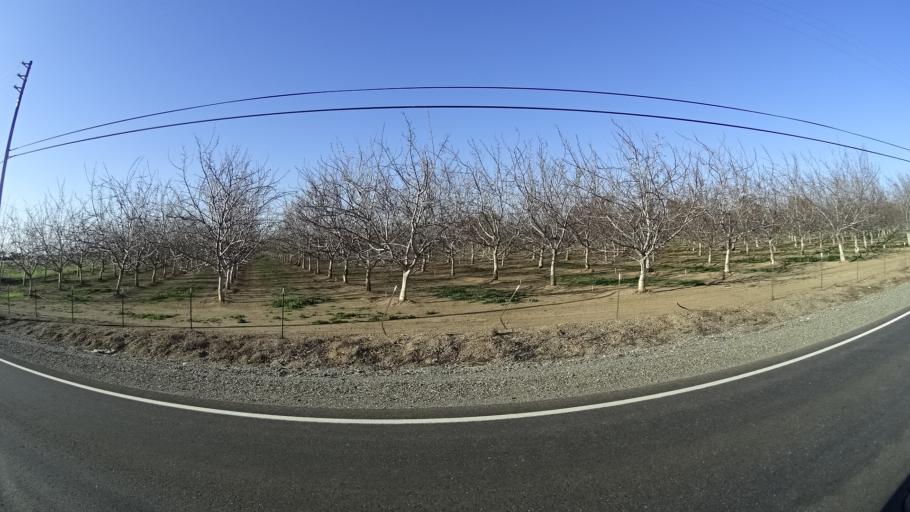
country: US
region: California
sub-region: Glenn County
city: Orland
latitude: 39.7764
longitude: -122.2763
